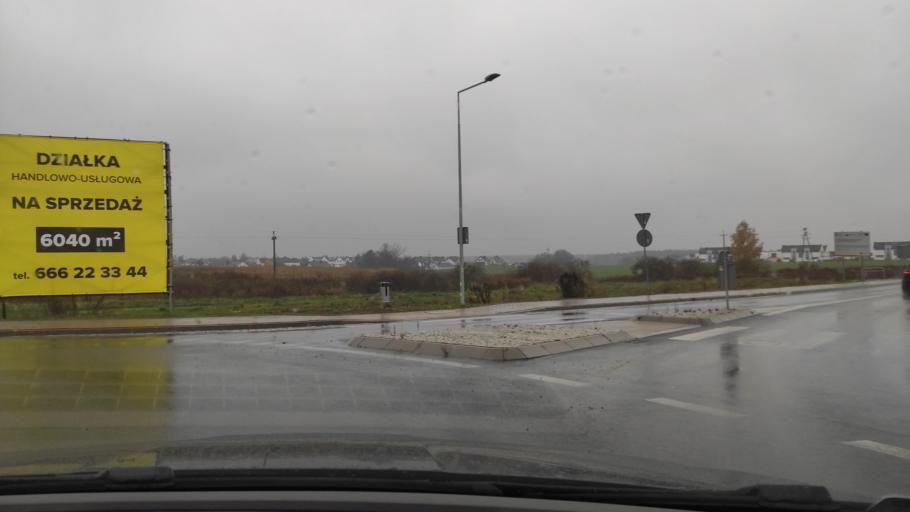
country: PL
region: Greater Poland Voivodeship
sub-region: Powiat poznanski
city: Swarzedz
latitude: 52.3806
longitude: 17.0718
